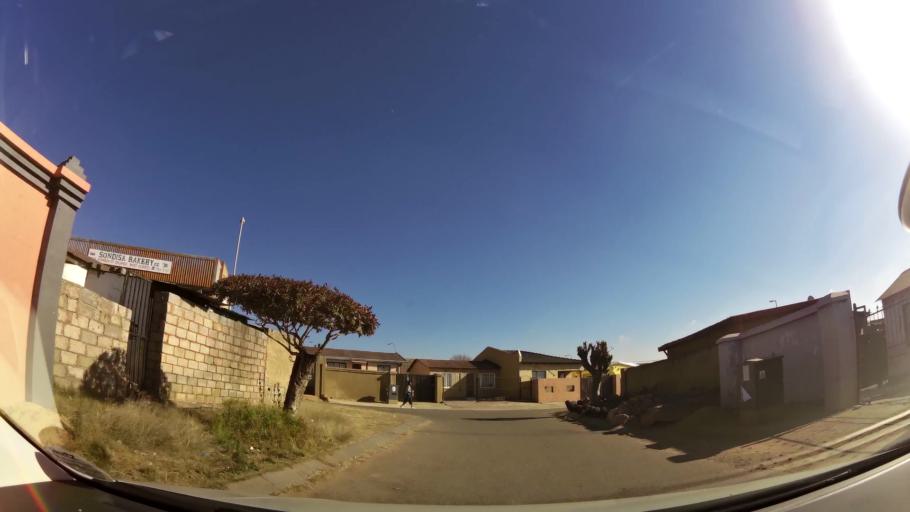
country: ZA
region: Gauteng
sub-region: City of Johannesburg Metropolitan Municipality
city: Roodepoort
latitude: -26.2204
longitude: 27.9194
